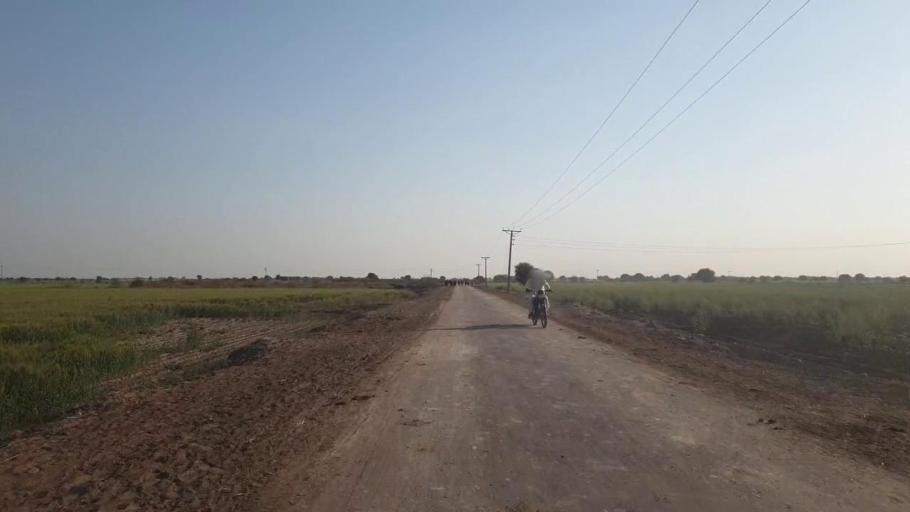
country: PK
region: Sindh
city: Chambar
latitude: 25.2855
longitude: 68.7498
